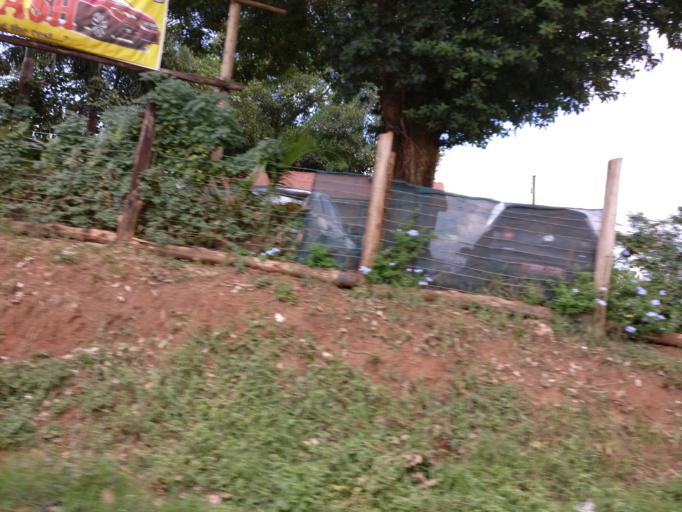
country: UG
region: Central Region
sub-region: Kampala District
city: Kampala
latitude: 0.2845
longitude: 32.5646
